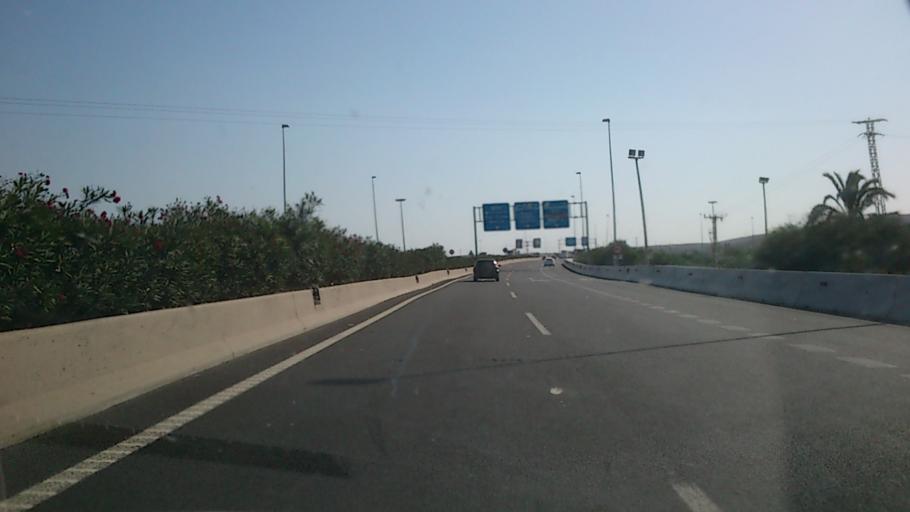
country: ES
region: Valencia
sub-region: Provincia de Alicante
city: San Vicent del Raspeig
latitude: 38.3431
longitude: -0.5423
